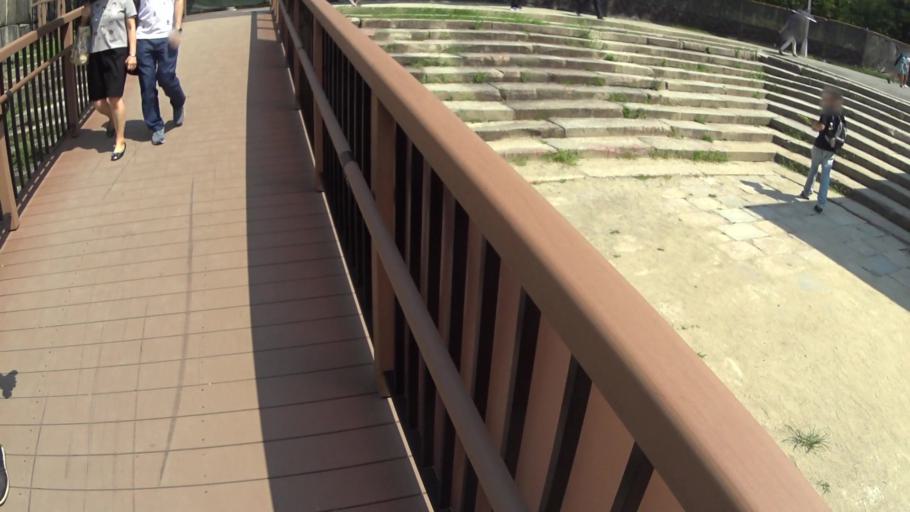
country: JP
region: Osaka
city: Osaka-shi
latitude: 34.6885
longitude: 135.5266
